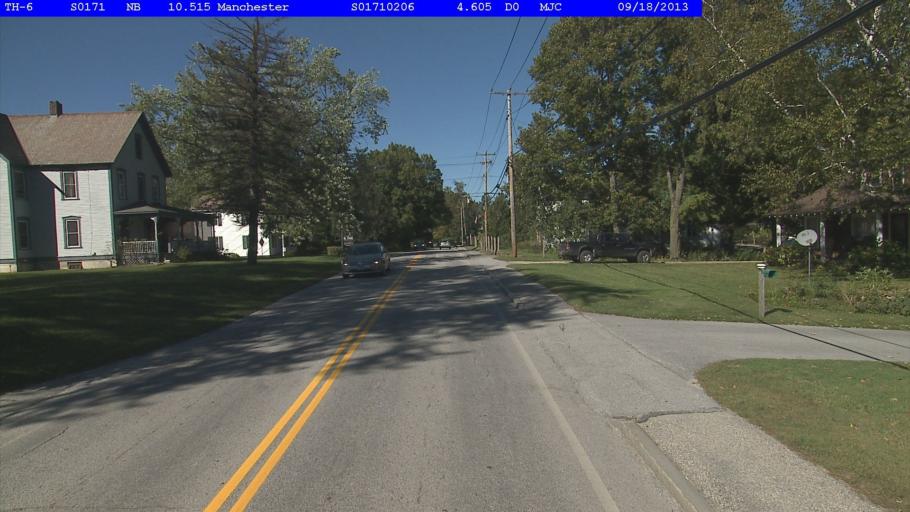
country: US
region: Vermont
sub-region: Bennington County
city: Manchester Center
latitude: 43.1690
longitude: -73.0487
